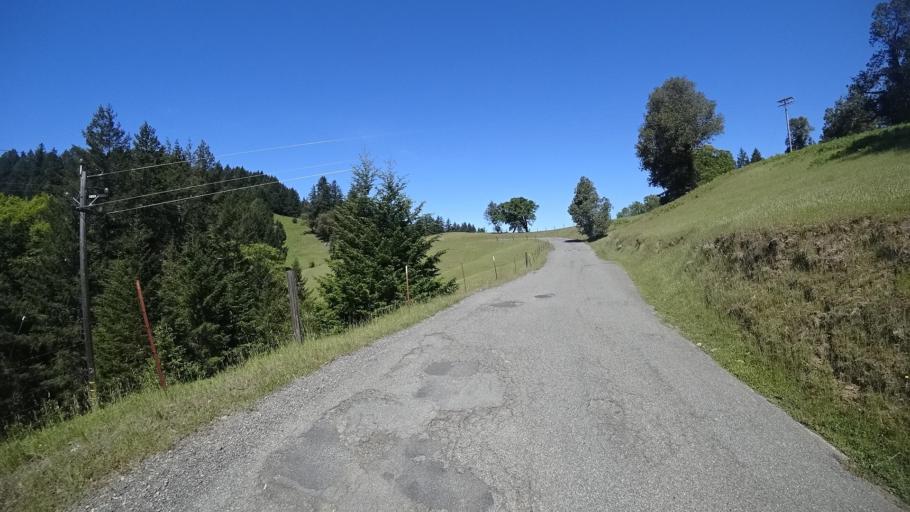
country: US
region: California
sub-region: Humboldt County
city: Redway
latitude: 40.1444
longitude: -124.0095
